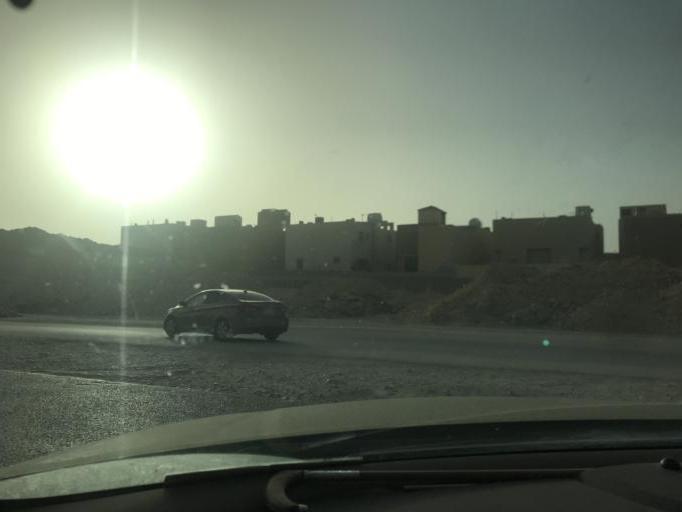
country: SA
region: Ar Riyad
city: Riyadh
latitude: 24.8384
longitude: 46.6679
